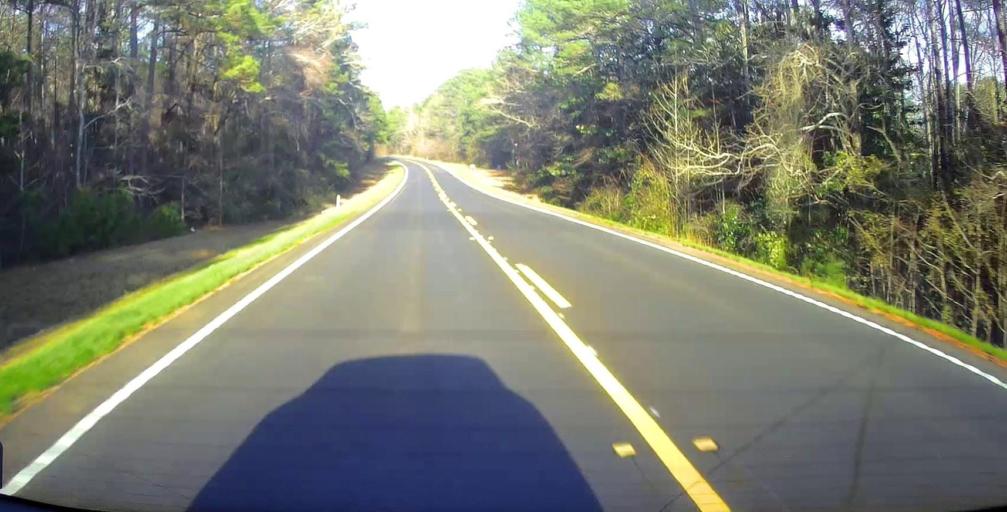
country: US
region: Georgia
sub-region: Harris County
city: Hamilton
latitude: 32.7438
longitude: -84.9457
